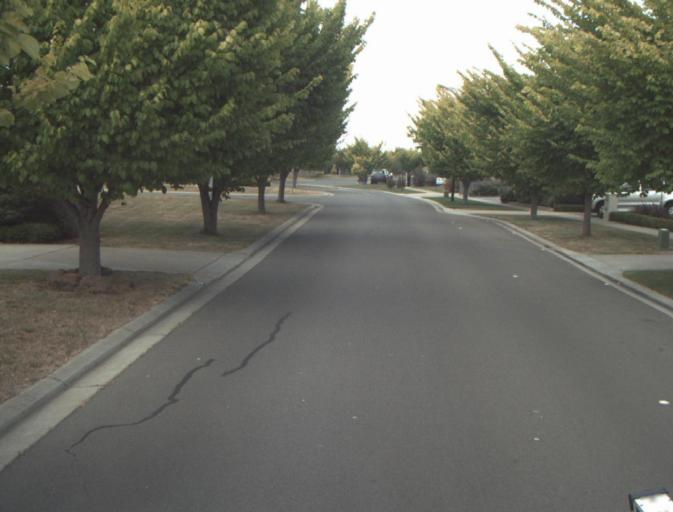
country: AU
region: Tasmania
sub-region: Launceston
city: East Launceston
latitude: -41.4335
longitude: 147.1580
